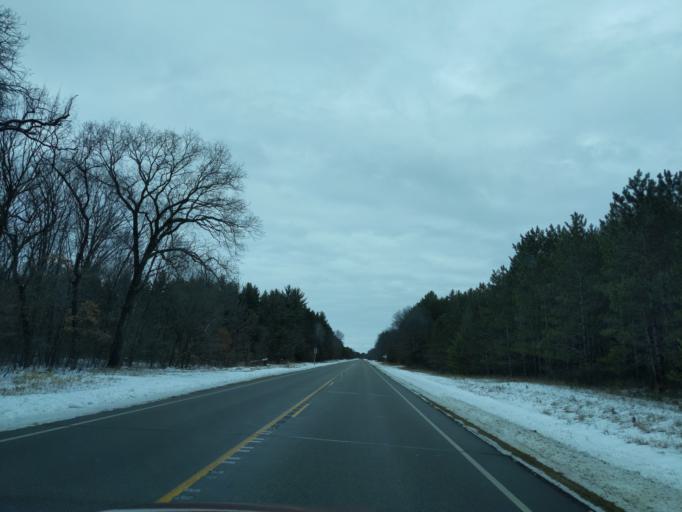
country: US
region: Wisconsin
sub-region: Marquette County
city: Montello
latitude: 43.9217
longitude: -89.3122
